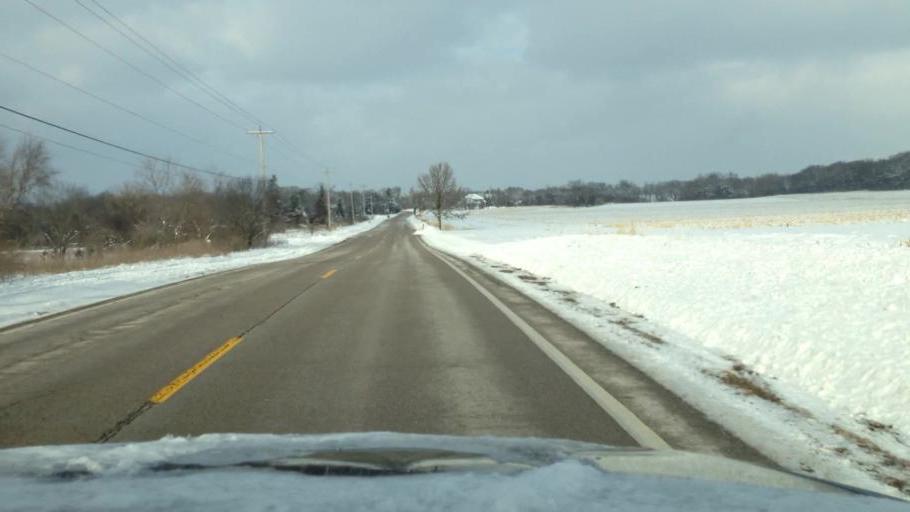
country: US
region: Wisconsin
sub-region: Waukesha County
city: Eagle
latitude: 42.8814
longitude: -88.4213
